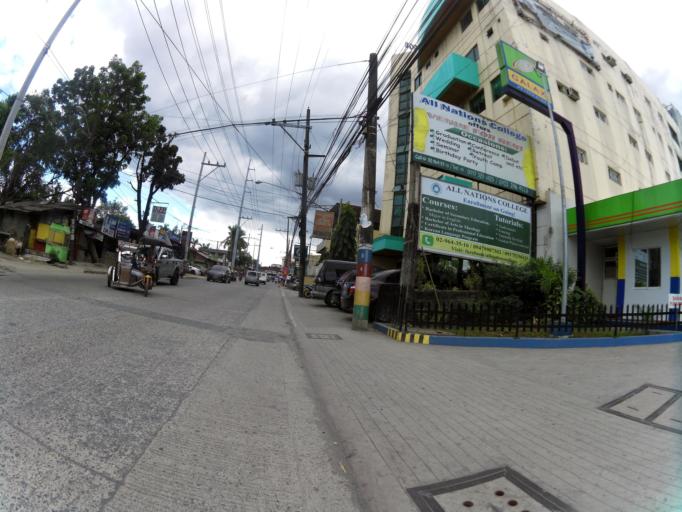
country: PH
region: Calabarzon
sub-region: Province of Rizal
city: Antipolo
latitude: 14.6309
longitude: 121.1218
